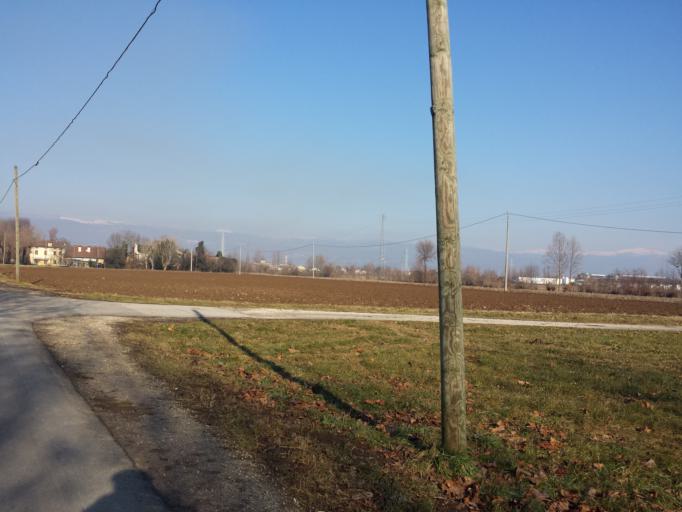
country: IT
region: Veneto
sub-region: Provincia di Vicenza
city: Sandrigo
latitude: 45.6419
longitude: 11.6023
